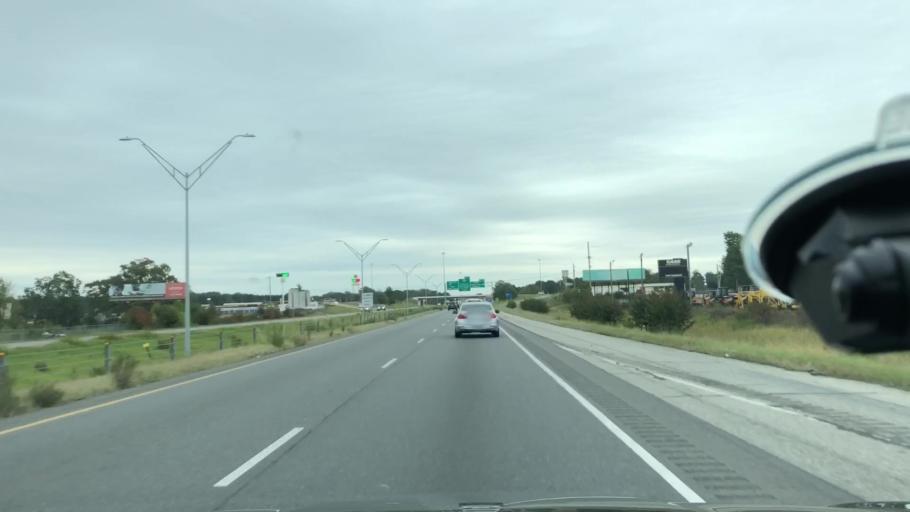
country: US
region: Arkansas
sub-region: Miller County
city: Texarkana
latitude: 33.4743
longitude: -94.0141
